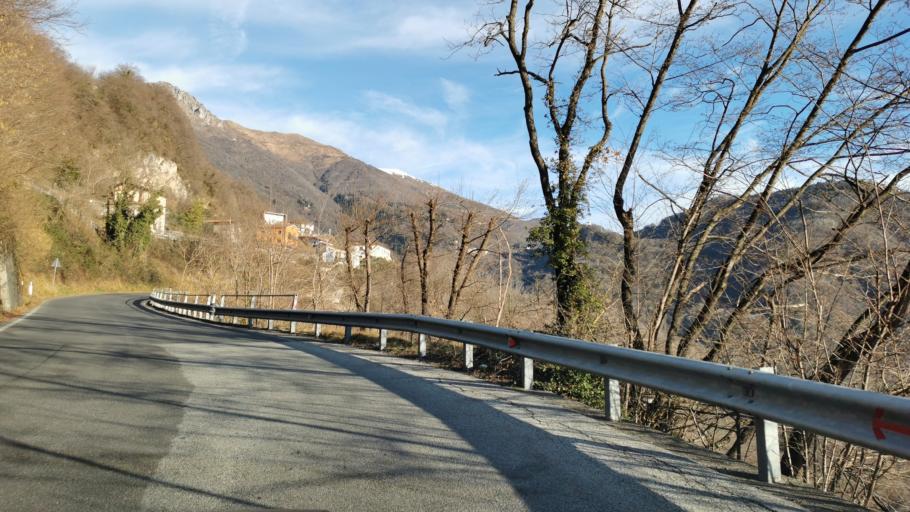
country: IT
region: Lombardy
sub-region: Provincia di Como
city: Plesio
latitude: 46.0333
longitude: 9.2316
